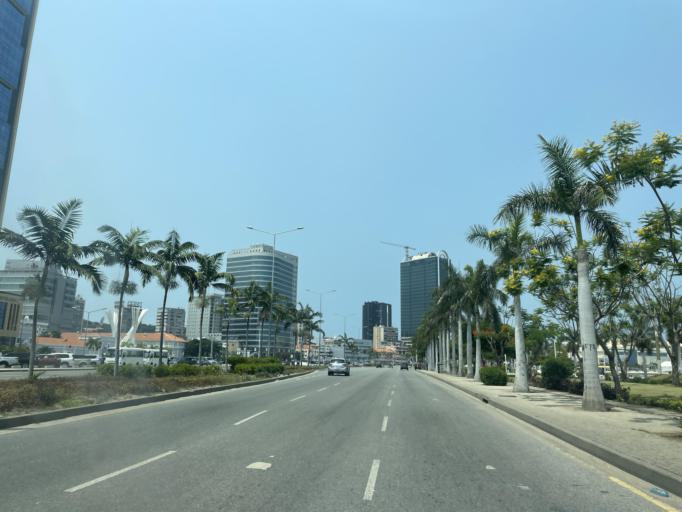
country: AO
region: Luanda
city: Luanda
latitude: -8.8103
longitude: 13.2323
